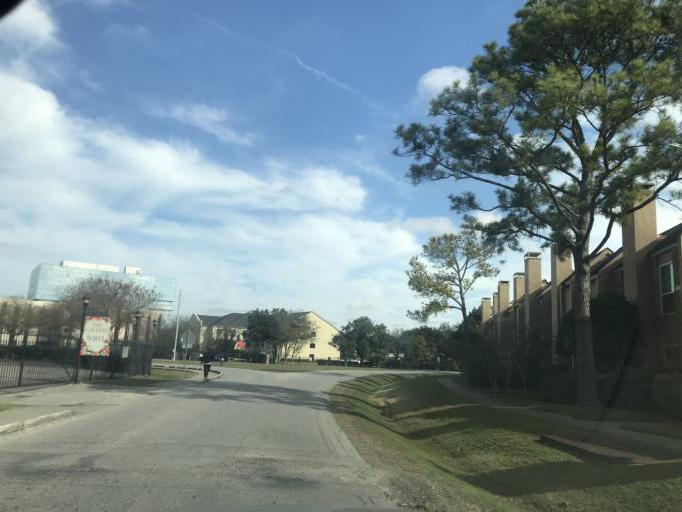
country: US
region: Texas
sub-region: Harris County
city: Piney Point Village
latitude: 29.7298
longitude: -95.4921
